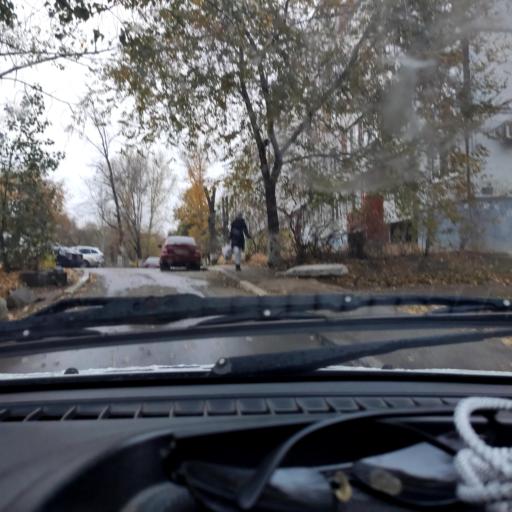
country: RU
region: Samara
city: Zhigulevsk
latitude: 53.4758
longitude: 49.5159
